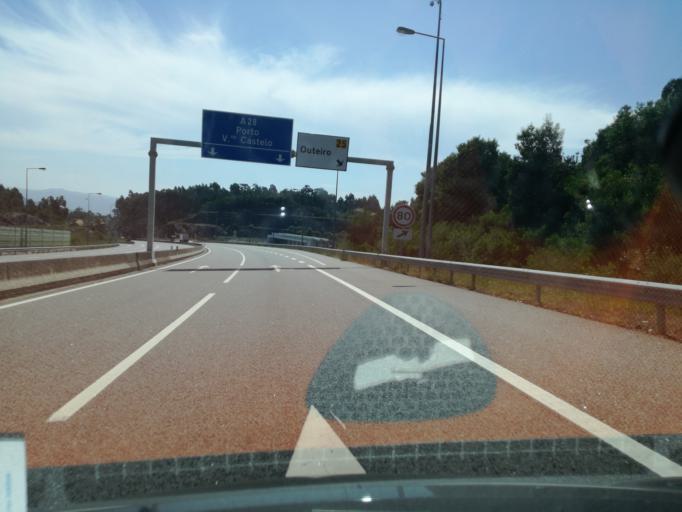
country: PT
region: Viana do Castelo
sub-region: Viana do Castelo
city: Meadela
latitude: 41.7443
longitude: -8.7986
